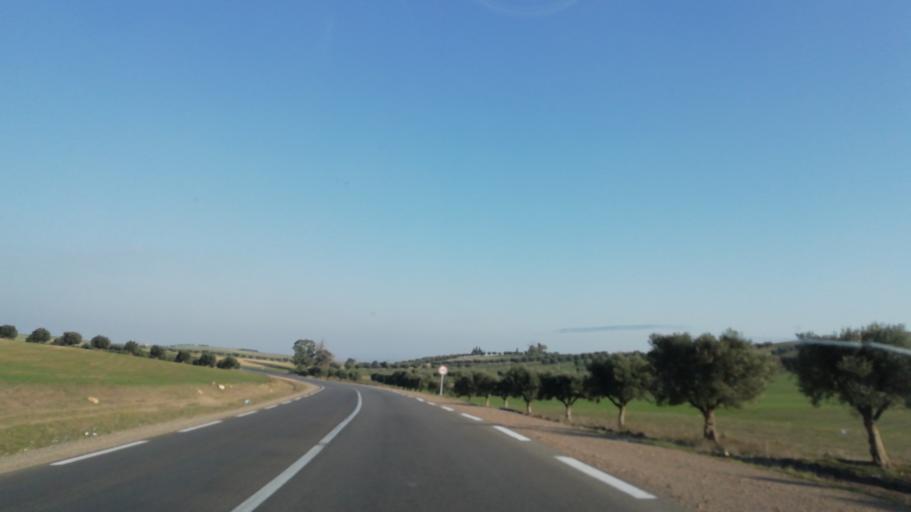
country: DZ
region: Ain Temouchent
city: Hammam Bou Hadjar
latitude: 35.1628
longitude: -0.8706
